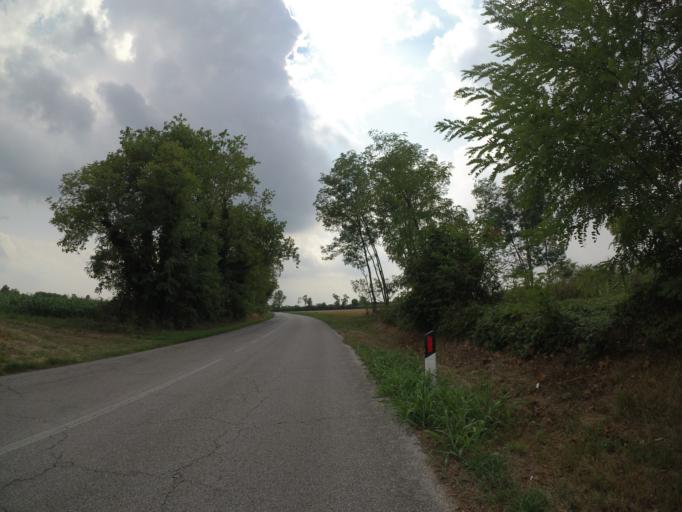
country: IT
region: Friuli Venezia Giulia
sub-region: Provincia di Udine
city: Sedegliano
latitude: 46.0114
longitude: 13.0062
